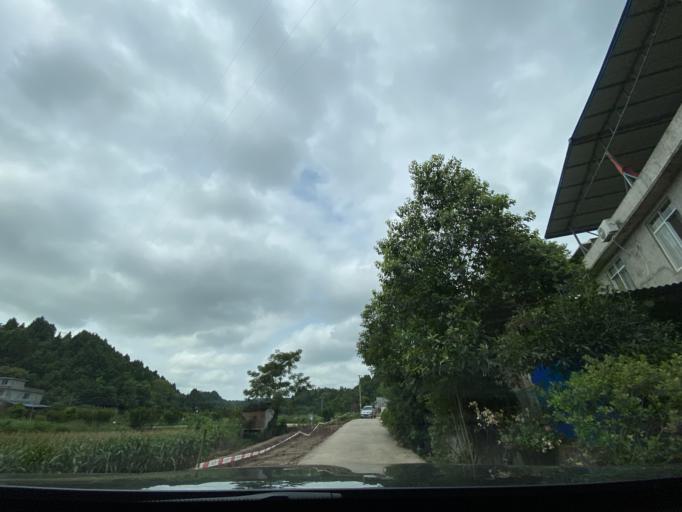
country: CN
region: Sichuan
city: Jiancheng
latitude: 30.4041
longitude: 104.5744
